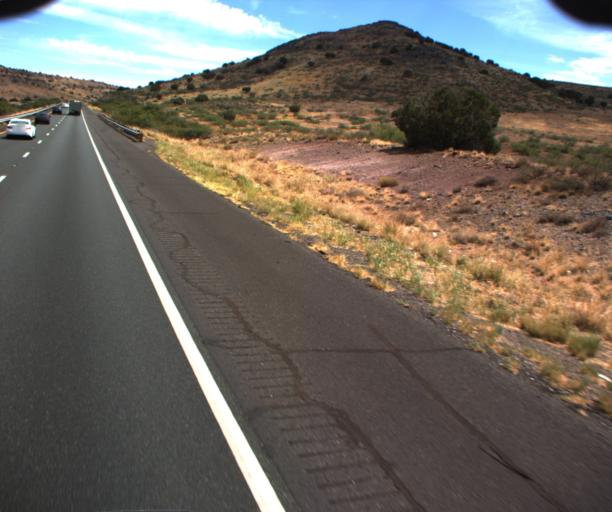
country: US
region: Arizona
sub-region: Yavapai County
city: Cordes Lakes
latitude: 34.4714
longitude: -112.0229
